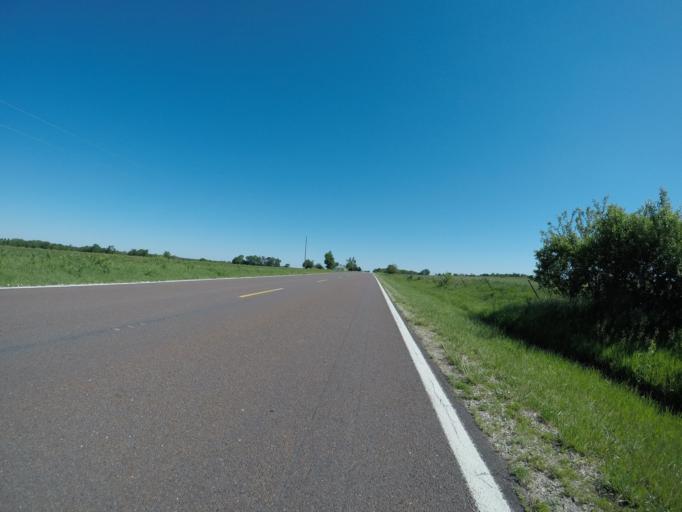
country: US
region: Kansas
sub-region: Osage County
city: Osage City
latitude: 38.7296
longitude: -96.0940
